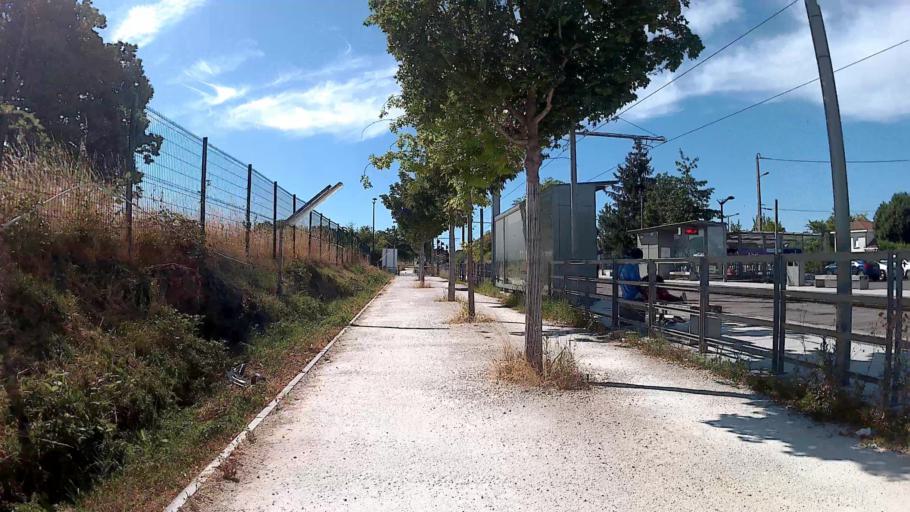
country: FR
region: Aquitaine
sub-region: Departement de la Gironde
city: Le Bouscat
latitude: 44.8721
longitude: -0.5905
